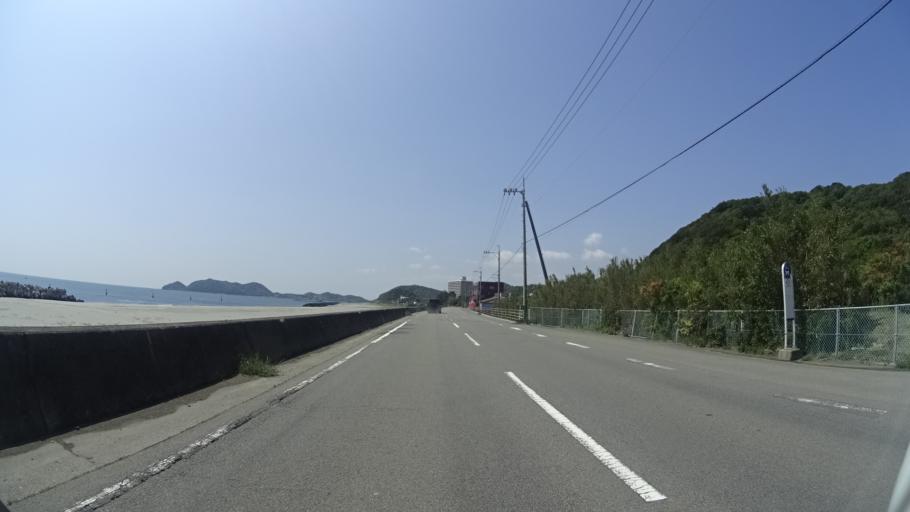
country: JP
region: Tokushima
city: Narutocho-mitsuishi
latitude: 34.2049
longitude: 134.6262
